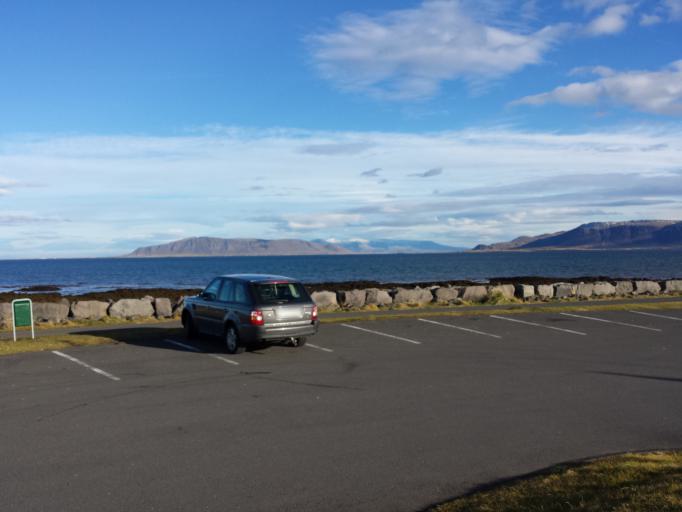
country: IS
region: Capital Region
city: Seltjarnarnes
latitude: 64.1625
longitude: -22.0137
